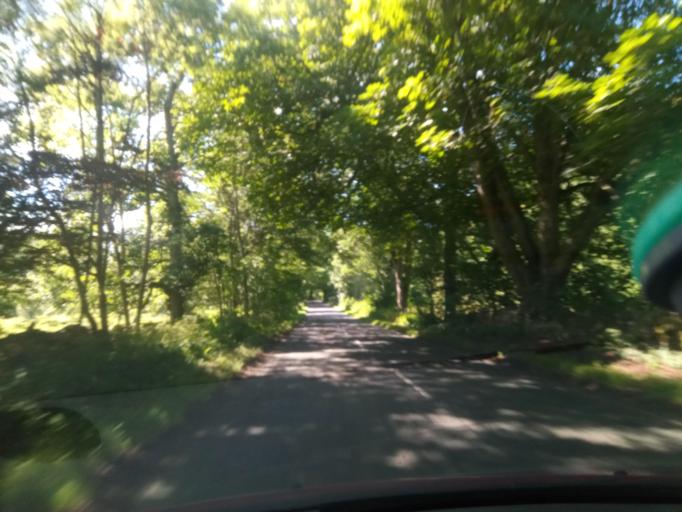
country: GB
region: England
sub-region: Northumberland
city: Bardon Mill
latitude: 54.9215
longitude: -2.3209
